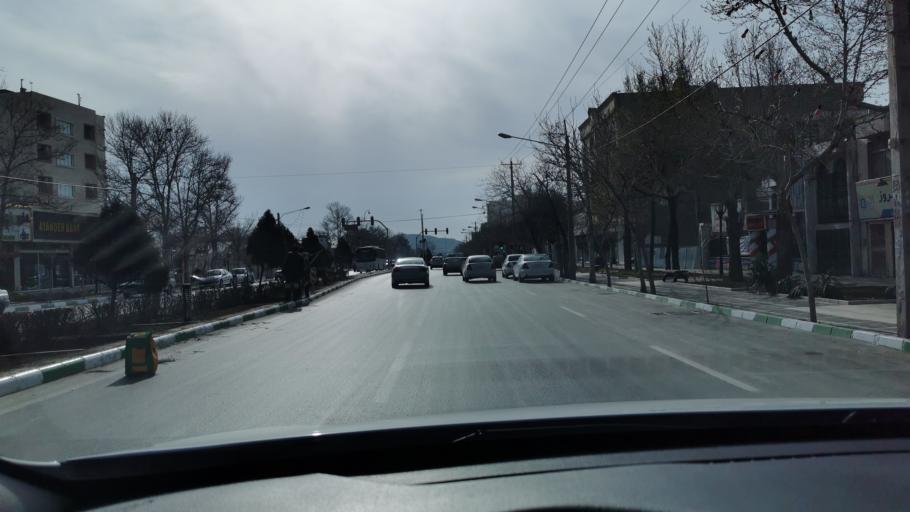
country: IR
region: Razavi Khorasan
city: Mashhad
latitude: 36.2879
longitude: 59.5428
